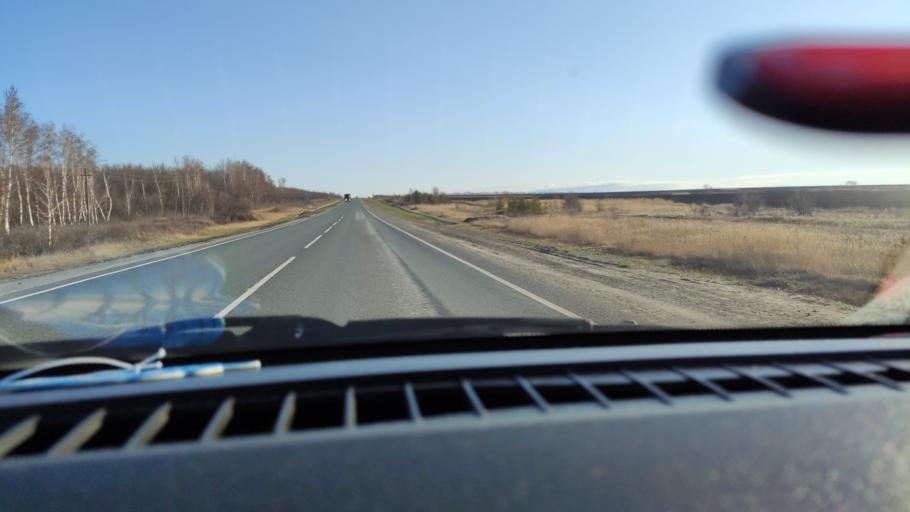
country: RU
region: Saratov
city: Alekseyevka
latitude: 52.2509
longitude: 47.9124
